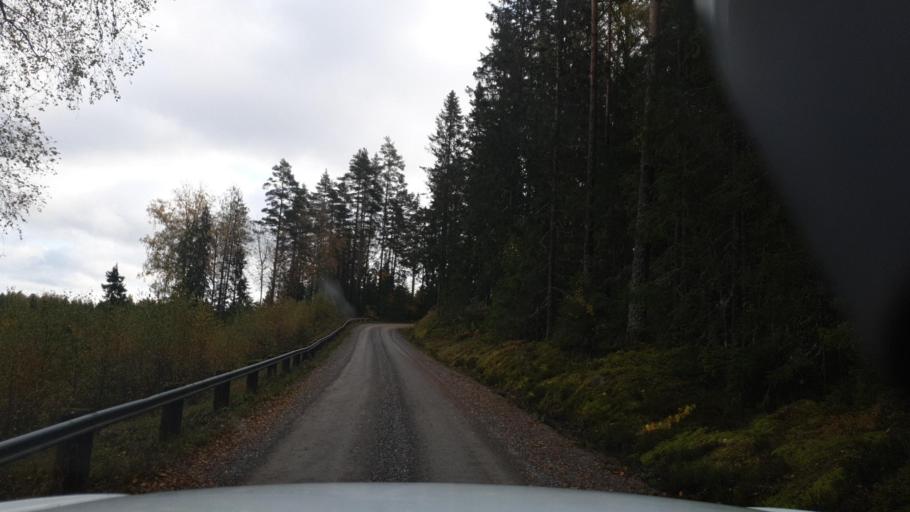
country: SE
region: Vaermland
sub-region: Arvika Kommun
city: Arvika
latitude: 59.5415
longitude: 12.4403
